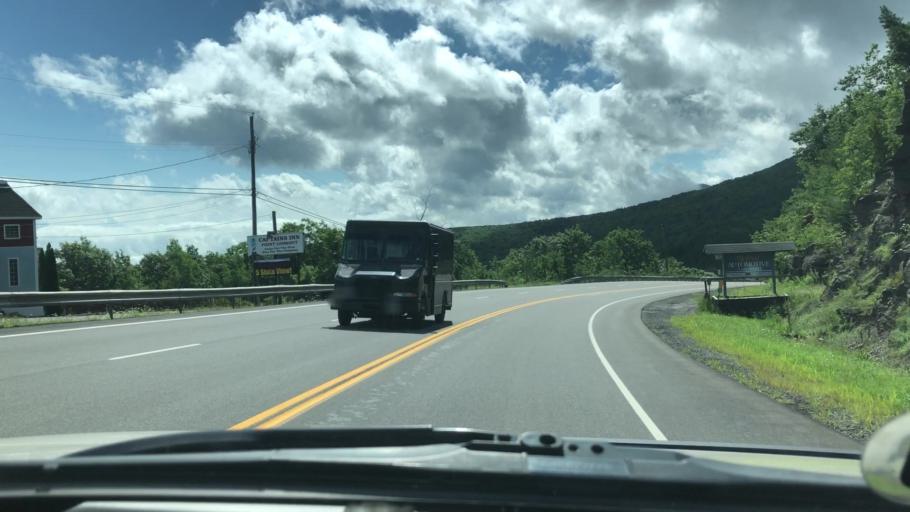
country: US
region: New York
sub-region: Greene County
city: Cairo
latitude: 42.3387
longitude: -74.1508
